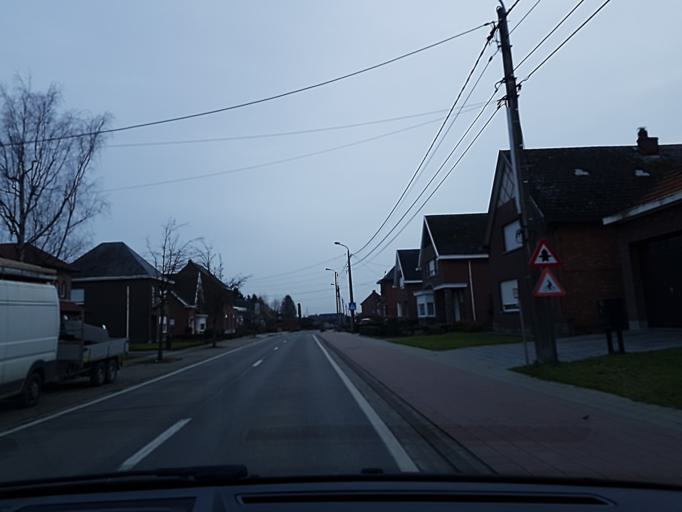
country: BE
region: Flanders
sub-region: Provincie Antwerpen
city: Putte
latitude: 51.0488
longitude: 4.6325
